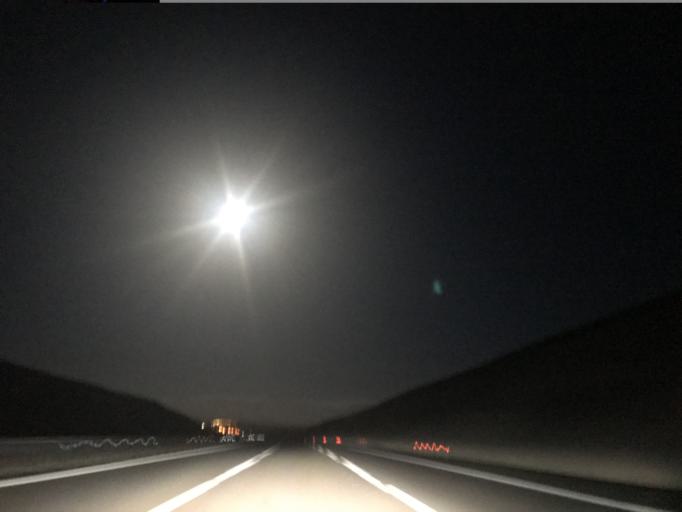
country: TR
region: Nigde
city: Ulukisla
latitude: 37.6352
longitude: 34.4126
